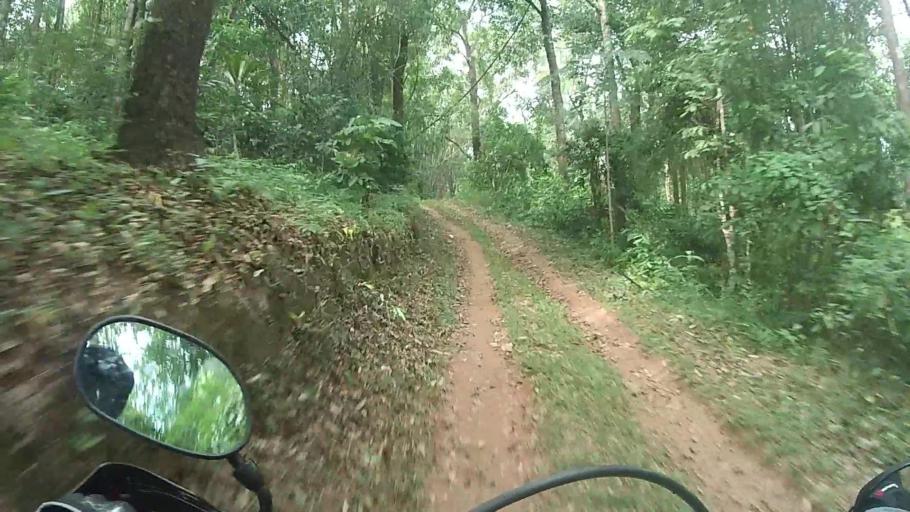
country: TH
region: Lampang
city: Mueang Pan
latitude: 18.8128
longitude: 99.3877
